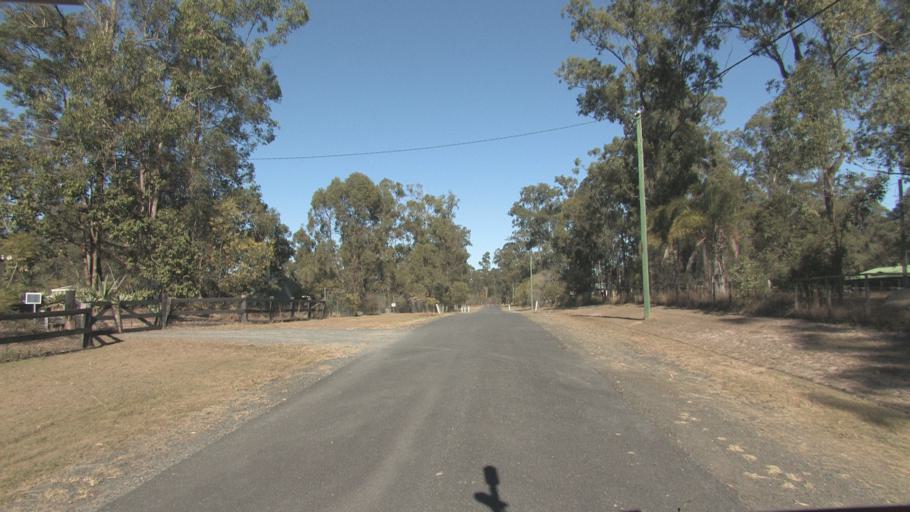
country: AU
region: Queensland
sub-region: Logan
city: North Maclean
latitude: -27.8085
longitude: 152.9675
